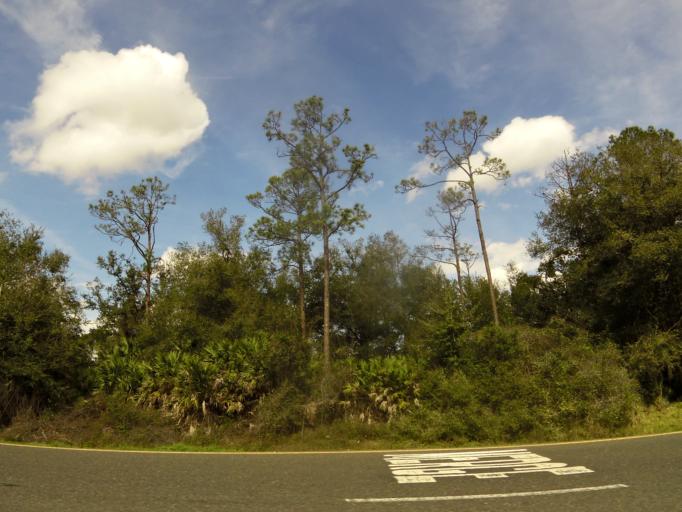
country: US
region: Florida
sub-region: Flagler County
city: Palm Coast
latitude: 29.5529
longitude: -81.2213
